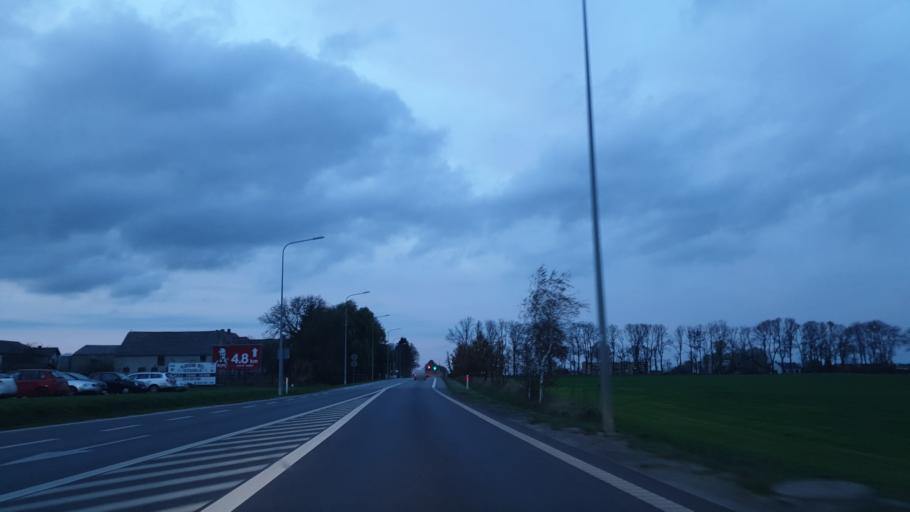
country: PL
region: Pomeranian Voivodeship
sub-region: Powiat pucki
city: Zelistrzewo
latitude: 54.6814
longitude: 18.3723
